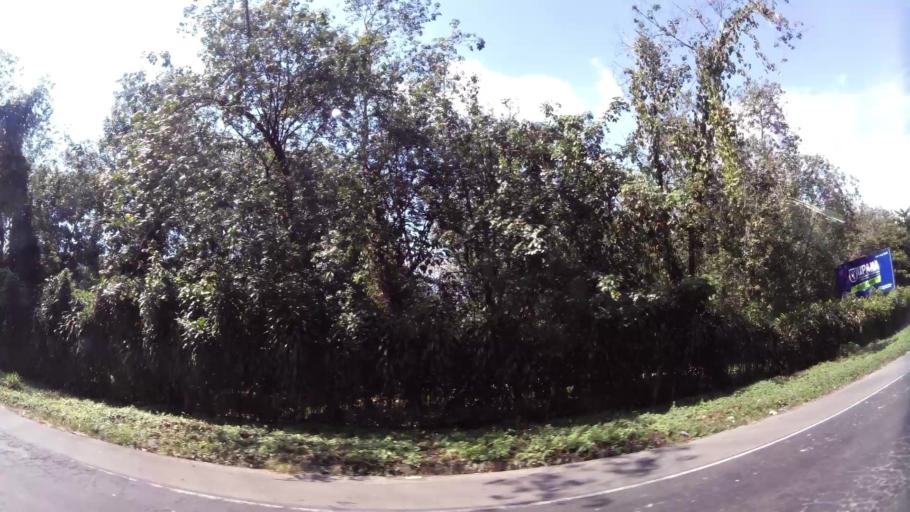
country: GT
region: Suchitepeque
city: Mazatenango
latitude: 14.5403
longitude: -91.4985
